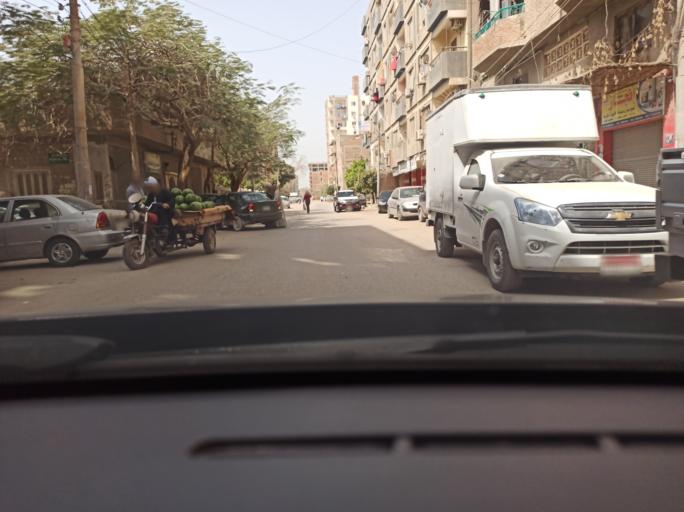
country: EG
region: Muhafazat Bani Suwayf
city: Bani Suwayf
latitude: 29.0826
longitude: 31.0905
